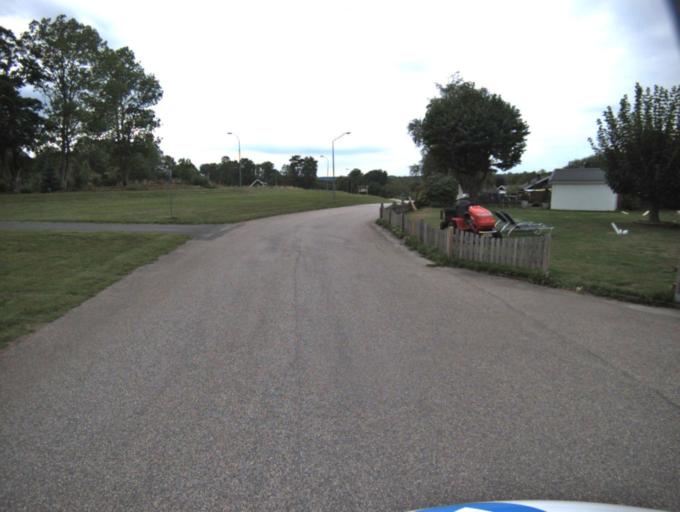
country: SE
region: Vaestra Goetaland
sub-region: Ulricehamns Kommun
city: Ulricehamn
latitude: 57.8378
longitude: 13.2904
